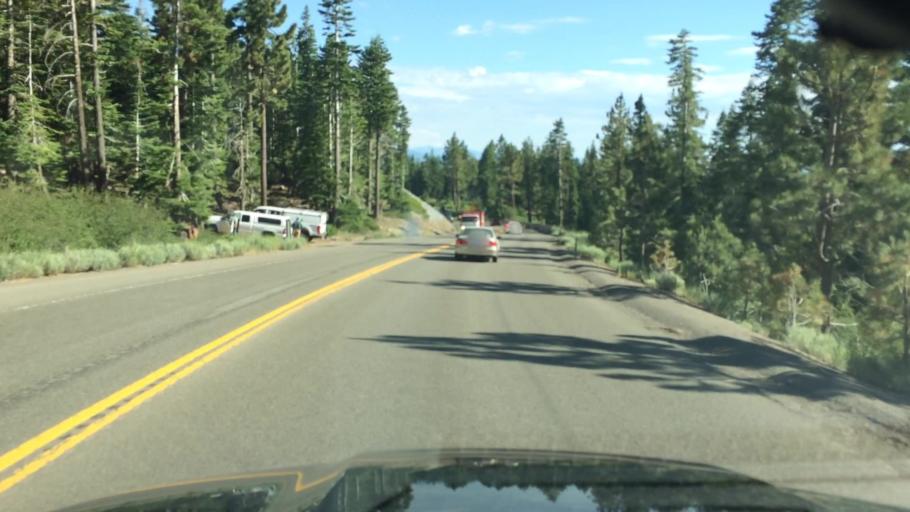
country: US
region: Nevada
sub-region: Washoe County
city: Incline Village
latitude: 39.2670
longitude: -119.9299
